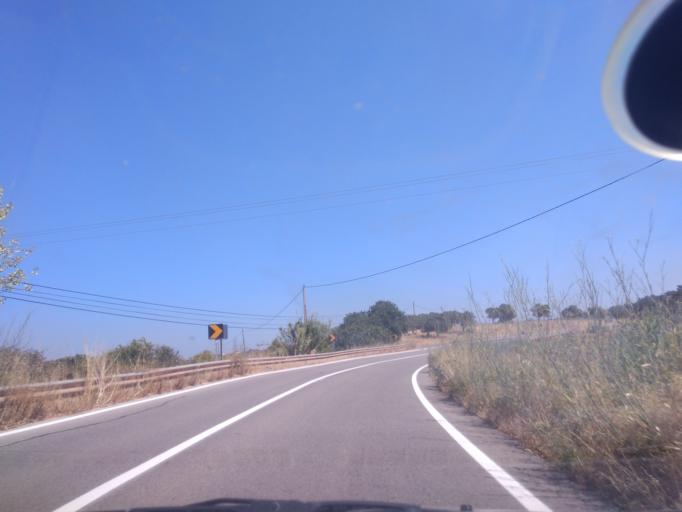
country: PT
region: Faro
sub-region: Lagos
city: Lagos
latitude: 37.1283
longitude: -8.6954
